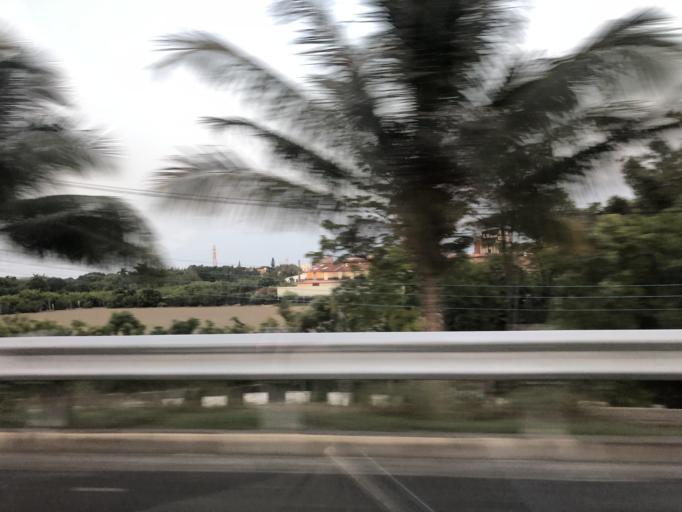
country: TW
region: Taiwan
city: Xinying
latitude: 23.3085
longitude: 120.2928
